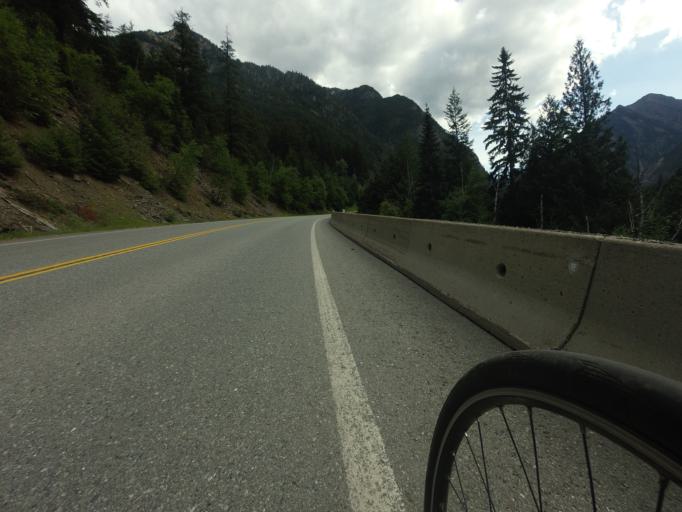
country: CA
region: British Columbia
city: Lillooet
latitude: 50.6353
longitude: -122.0888
